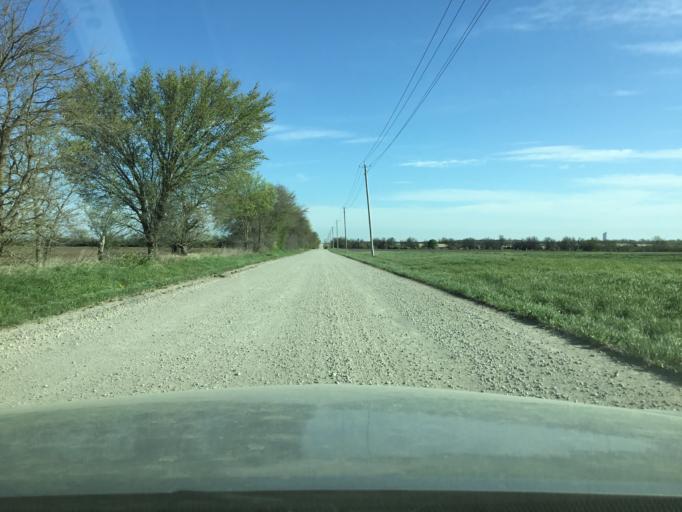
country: US
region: Kansas
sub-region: Neosho County
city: Chanute
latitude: 37.6485
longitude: -95.4893
